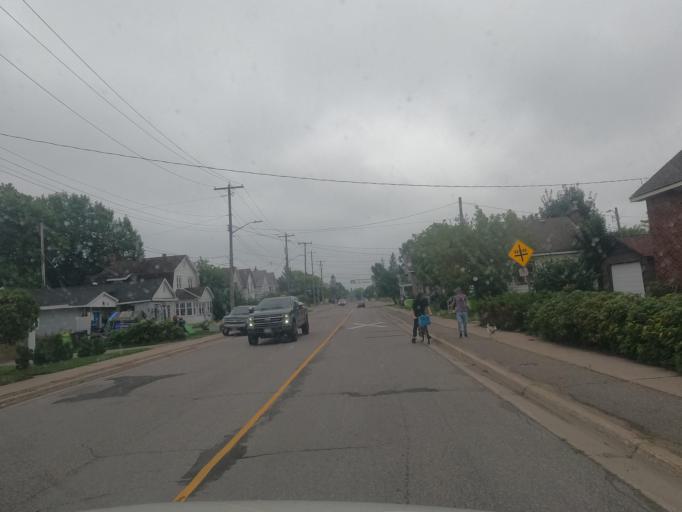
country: CA
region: Ontario
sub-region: Algoma
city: Sault Ste. Marie
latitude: 46.5245
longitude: -84.3464
